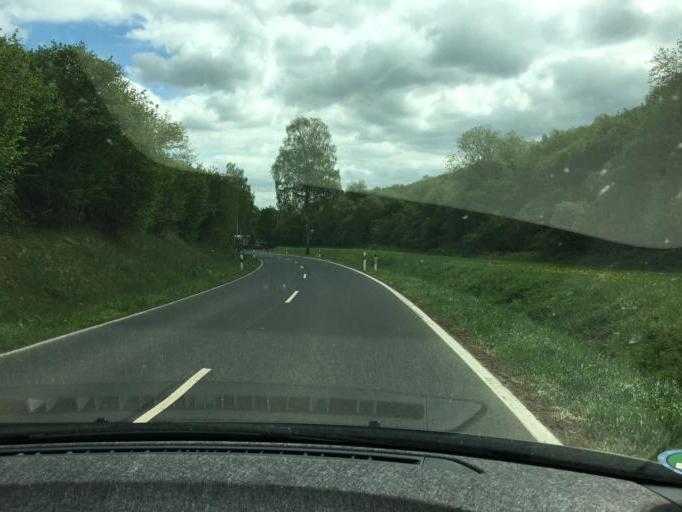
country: DE
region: North Rhine-Westphalia
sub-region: Regierungsbezirk Koln
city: Bad Munstereifel
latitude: 50.5840
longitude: 6.7586
